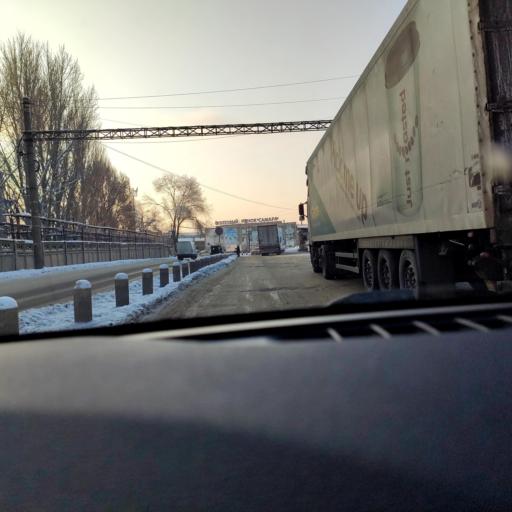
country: RU
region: Samara
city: Samara
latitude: 53.1936
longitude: 50.2360
